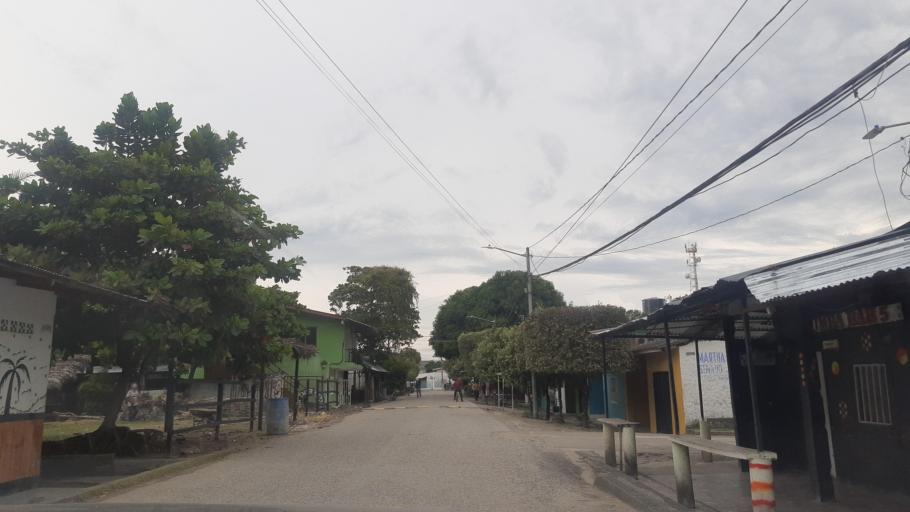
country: CO
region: Antioquia
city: Puerto Triunfo
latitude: 5.8736
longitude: -74.6393
